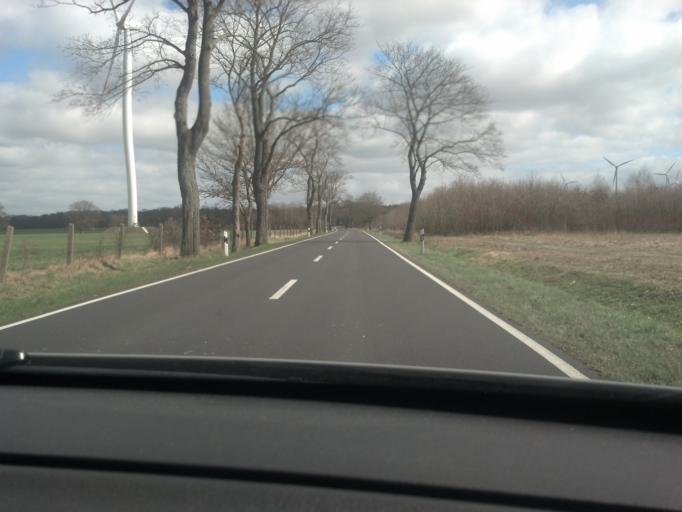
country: DE
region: Brandenburg
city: Gerdshagen
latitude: 53.2950
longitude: 12.1872
